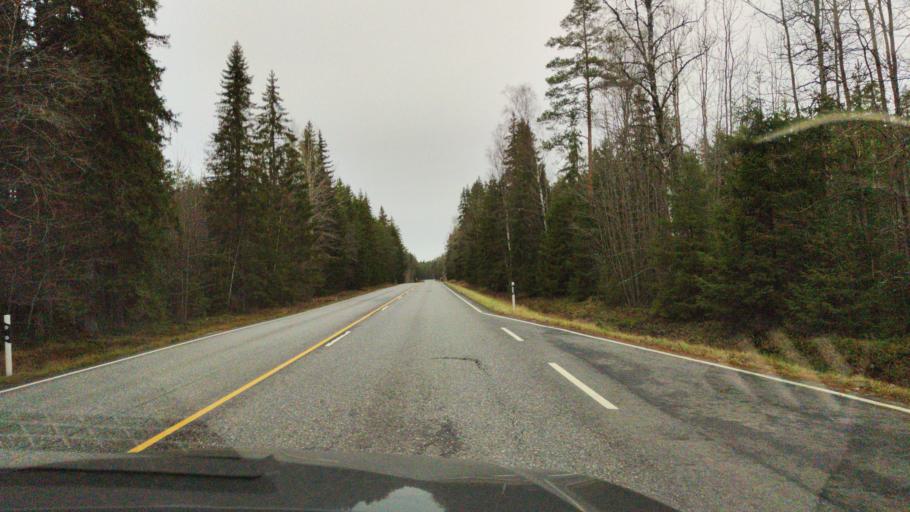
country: FI
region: Varsinais-Suomi
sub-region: Loimaa
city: Ylaene
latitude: 60.7306
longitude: 22.4379
